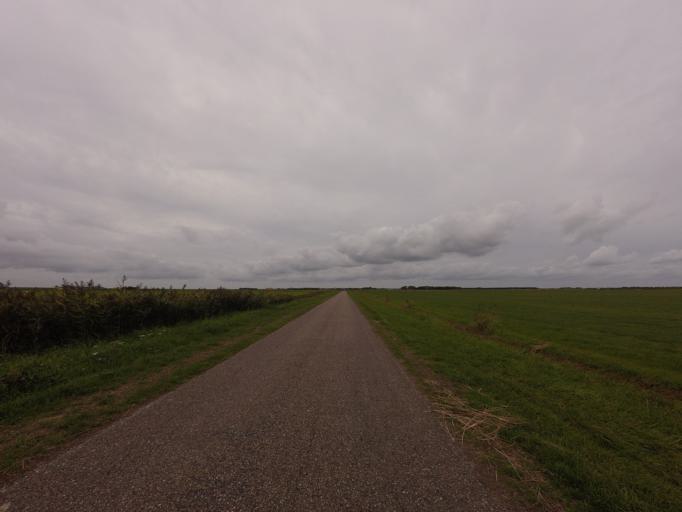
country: NL
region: Friesland
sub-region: Gemeente Ameland
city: Hollum
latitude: 53.4323
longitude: 5.6859
